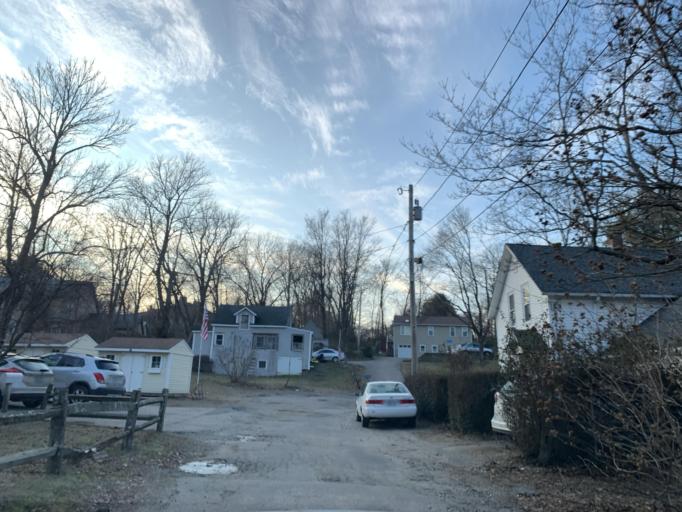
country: US
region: Rhode Island
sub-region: Washington County
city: Wakefield-Peacedale
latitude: 41.4503
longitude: -71.5017
